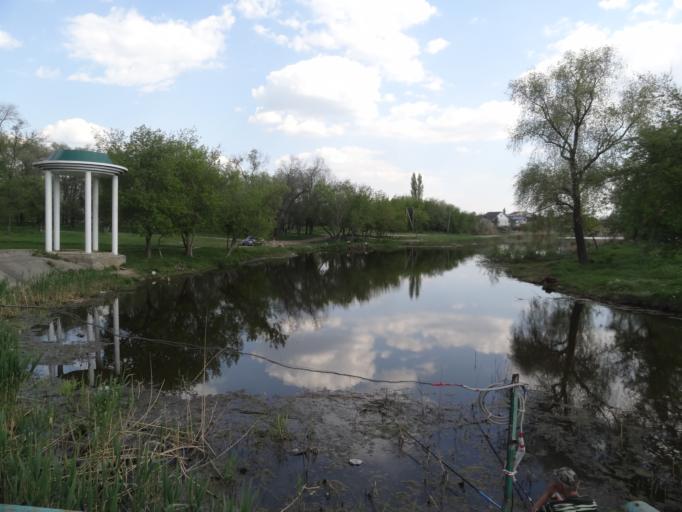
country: RU
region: Saratov
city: Engel's
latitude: 51.5006
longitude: 46.1018
